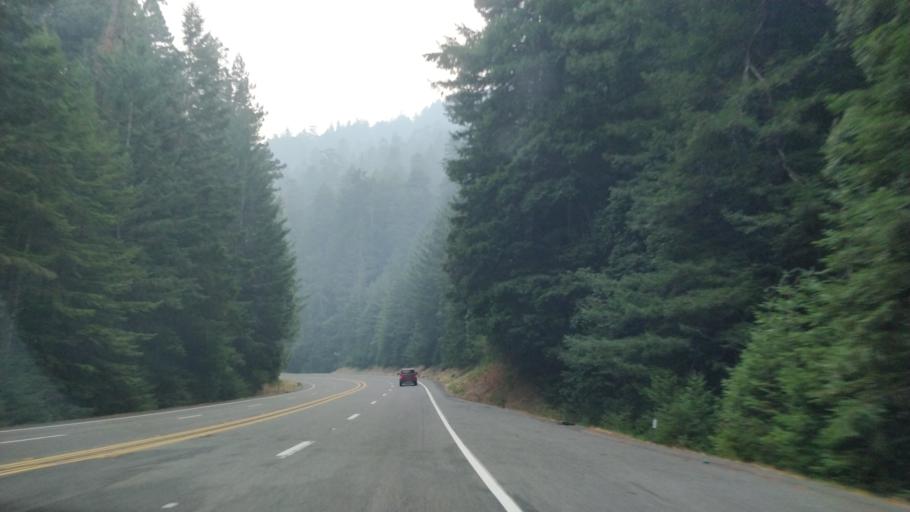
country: US
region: California
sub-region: Humboldt County
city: Rio Dell
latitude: 40.3732
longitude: -123.9264
